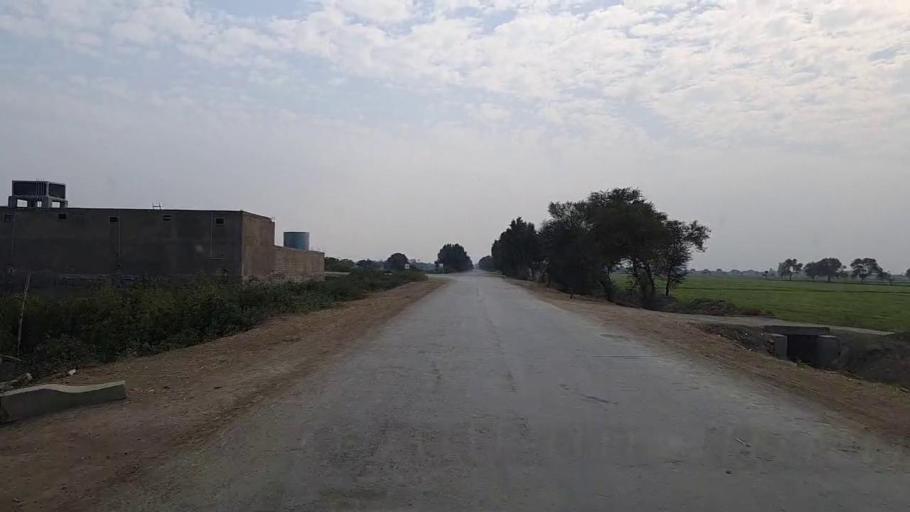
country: PK
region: Sindh
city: Mirwah Gorchani
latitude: 25.3822
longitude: 69.0818
